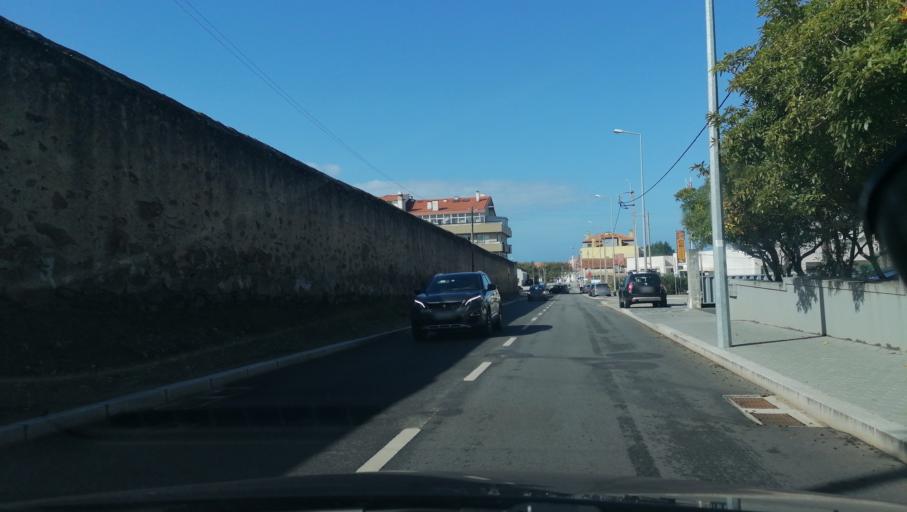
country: PT
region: Porto
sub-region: Vila Nova de Gaia
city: Arcozelo
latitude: 41.0404
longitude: -8.6441
